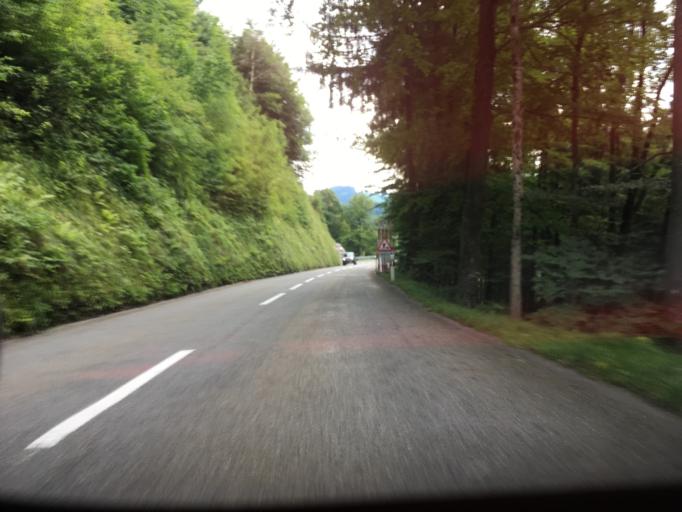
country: CH
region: Thurgau
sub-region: Muenchwilen District
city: Fischingen
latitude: 47.3592
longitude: 8.9633
